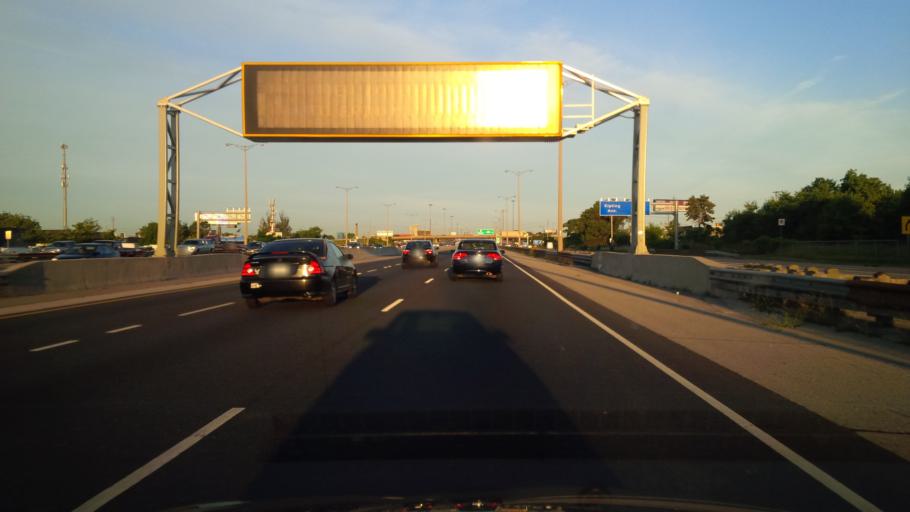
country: CA
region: Ontario
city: Etobicoke
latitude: 43.6194
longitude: -79.5190
